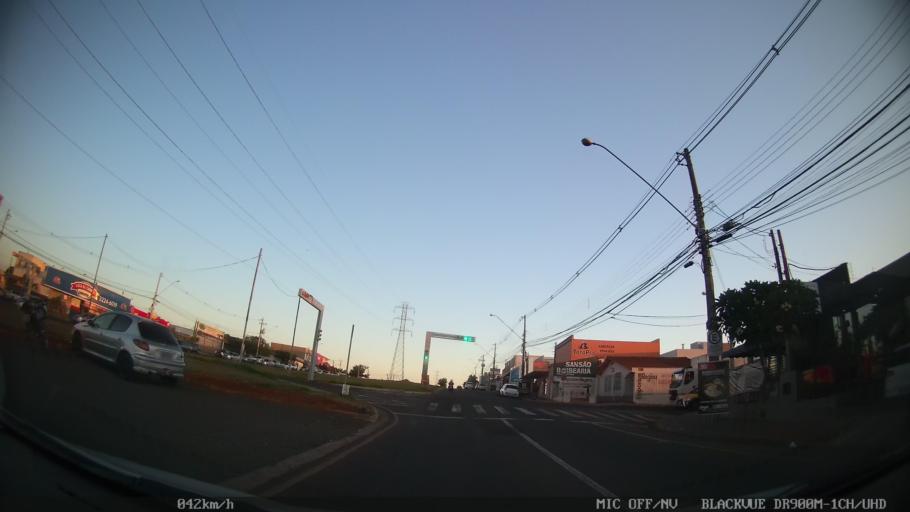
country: BR
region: Sao Paulo
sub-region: Sao Jose Do Rio Preto
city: Sao Jose do Rio Preto
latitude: -20.7893
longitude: -49.3442
